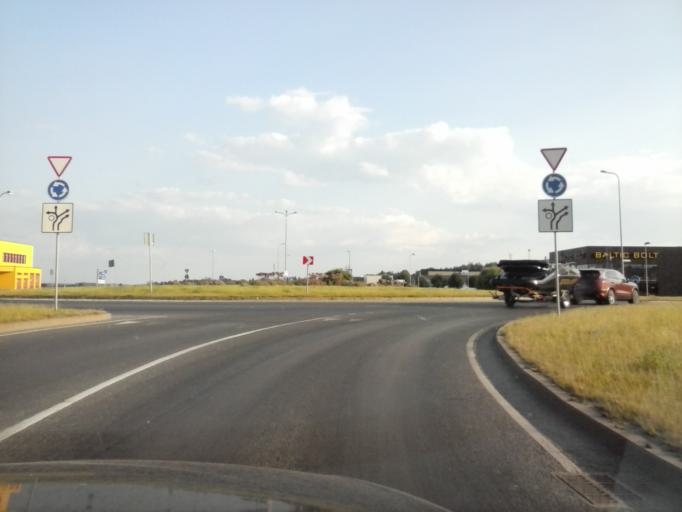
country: EE
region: Tartu
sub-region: UElenurme vald
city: Ulenurme
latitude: 58.3435
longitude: 26.7410
